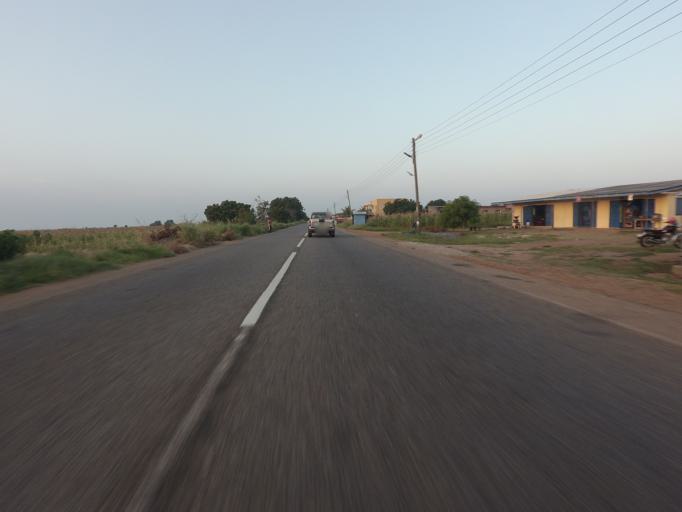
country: GH
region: Volta
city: Anloga
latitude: 5.8174
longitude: 0.9411
